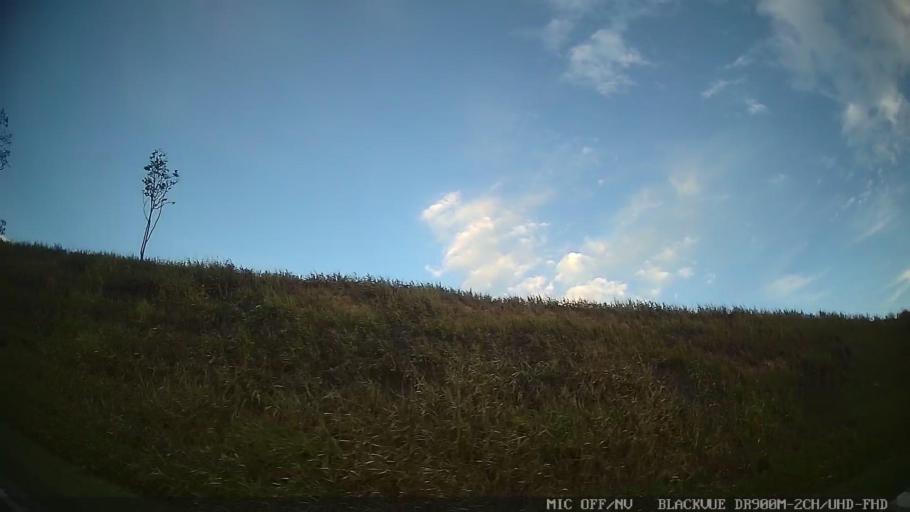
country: BR
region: Sao Paulo
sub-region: Salto
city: Salto
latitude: -23.1663
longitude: -47.2663
